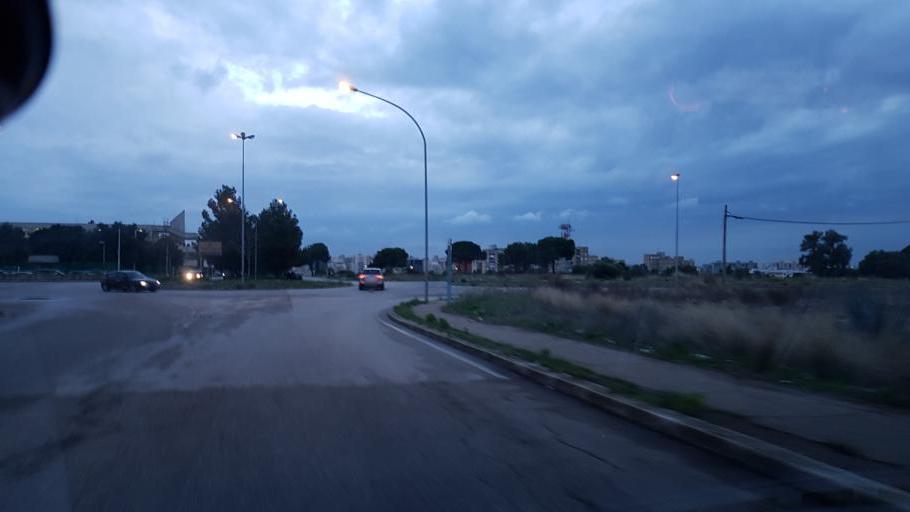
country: IT
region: Apulia
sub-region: Provincia di Taranto
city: Paolo VI
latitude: 40.5278
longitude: 17.2813
